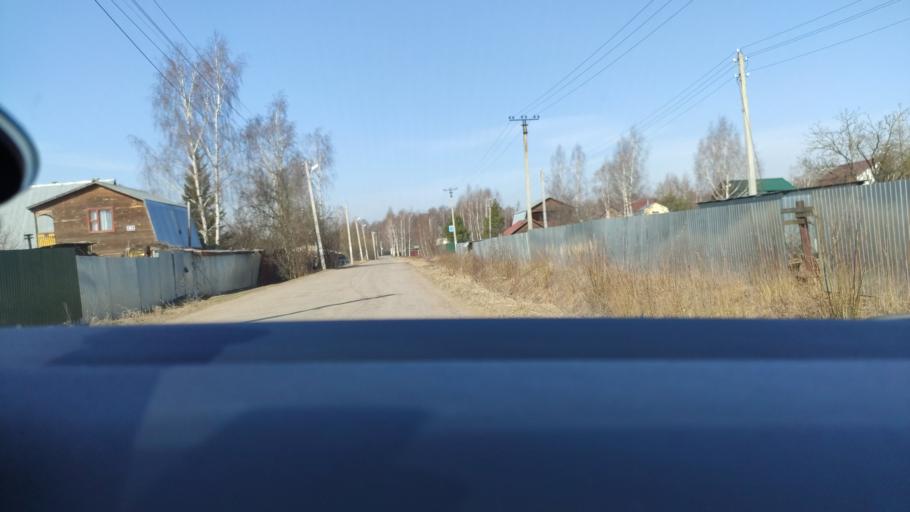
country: RU
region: Moskovskaya
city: Imeni Vorovskogo
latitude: 55.7806
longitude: 38.3659
